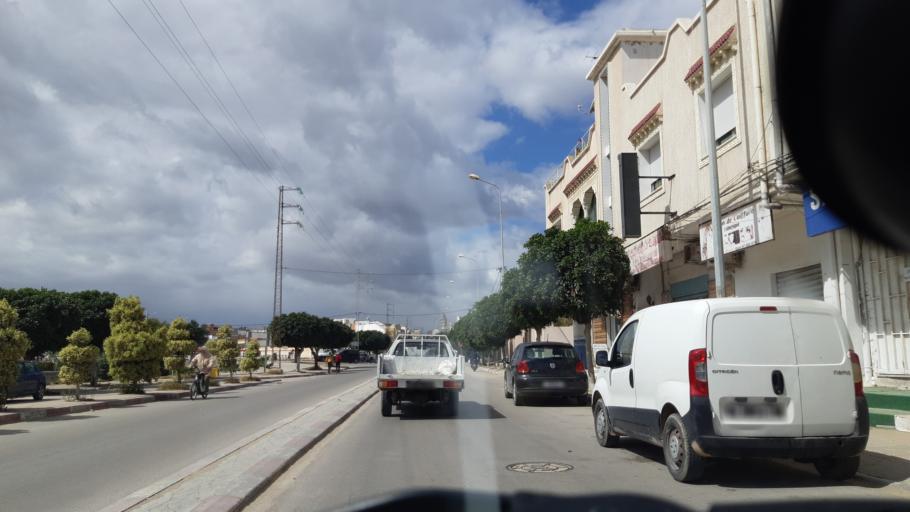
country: TN
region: Susah
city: Akouda
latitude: 35.8766
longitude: 10.5361
